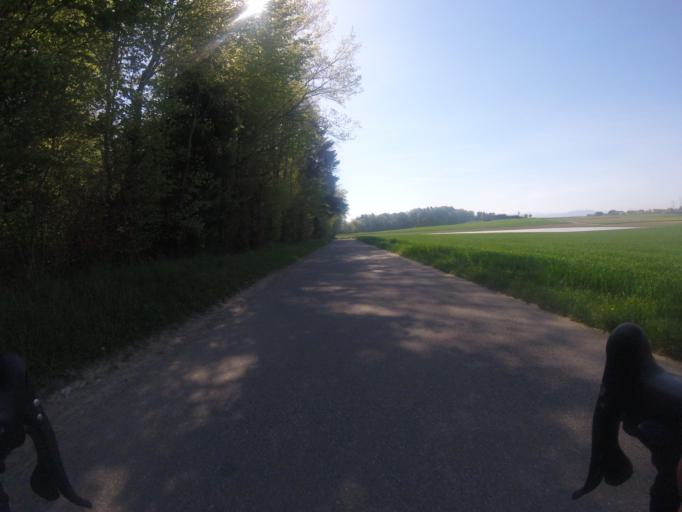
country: CH
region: Bern
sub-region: Bern-Mittelland District
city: Ferenbalm
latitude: 46.9379
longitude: 7.2276
